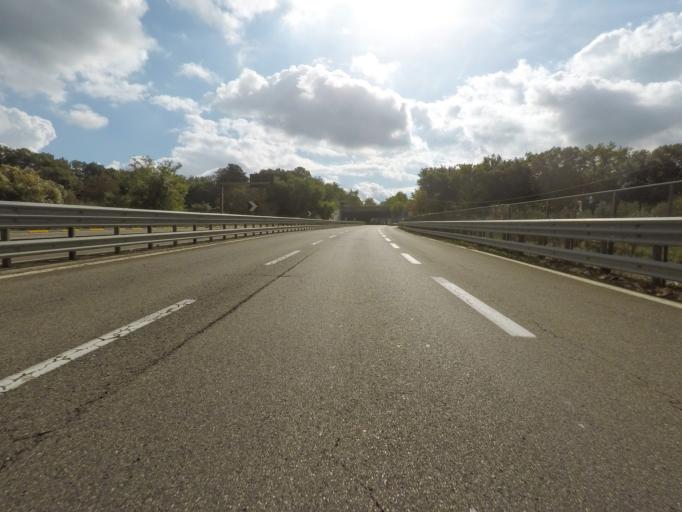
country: IT
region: Tuscany
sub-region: Provincia di Siena
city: Rapolano Terme
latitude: 43.3021
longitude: 11.5975
